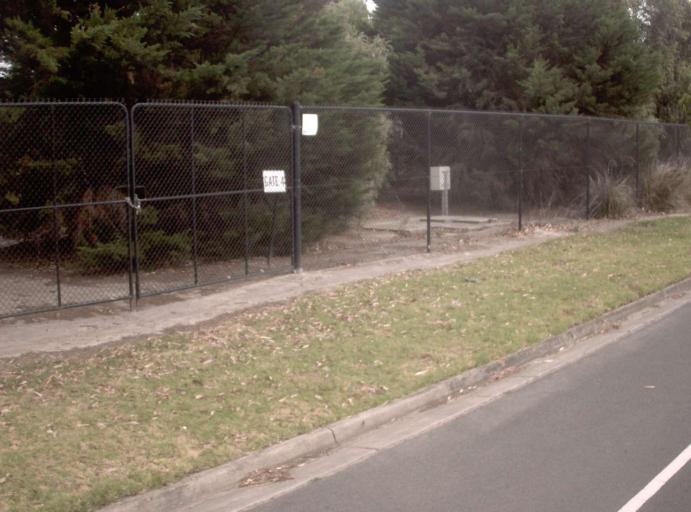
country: AU
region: Victoria
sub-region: Monash
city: Oakleigh South
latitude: -37.9227
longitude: 145.1013
